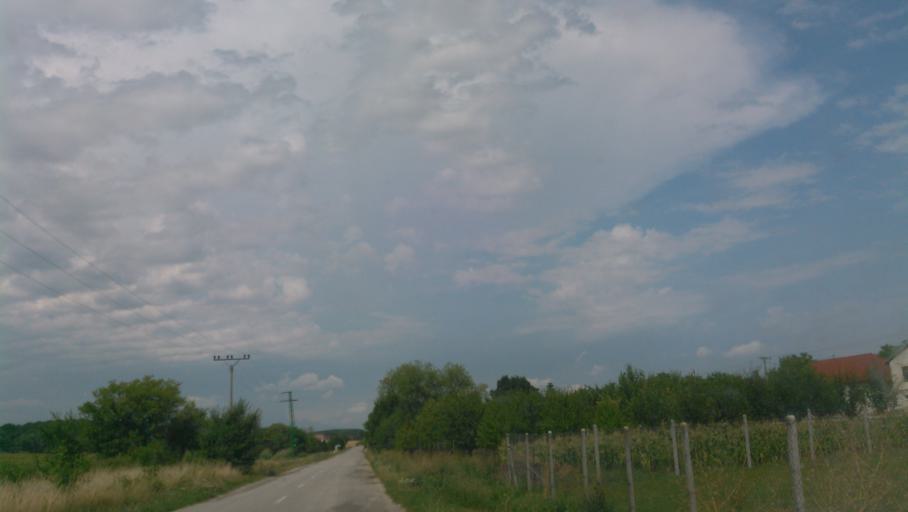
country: SK
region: Nitriansky
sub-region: Okres Nitra
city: Nitra
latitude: 48.4967
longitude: 18.0538
